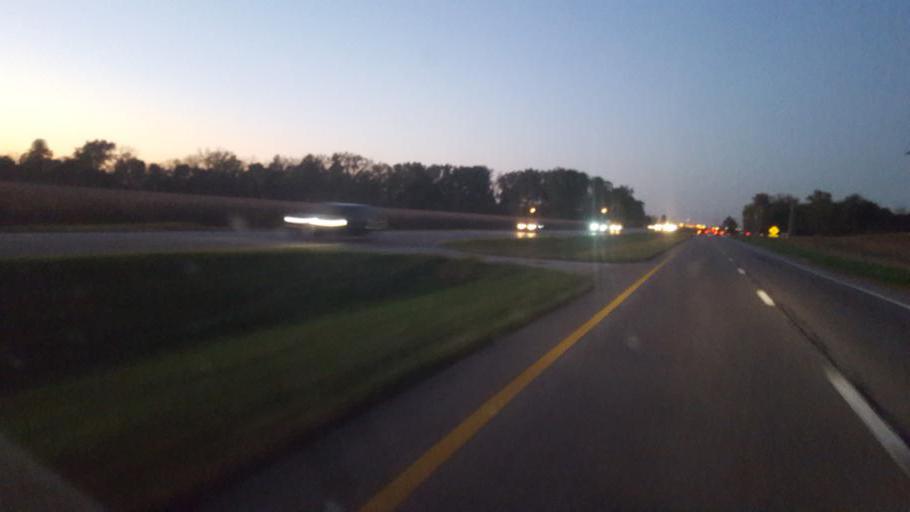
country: US
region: Ohio
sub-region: Pickaway County
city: Logan Elm Village
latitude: 39.5281
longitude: -82.9675
